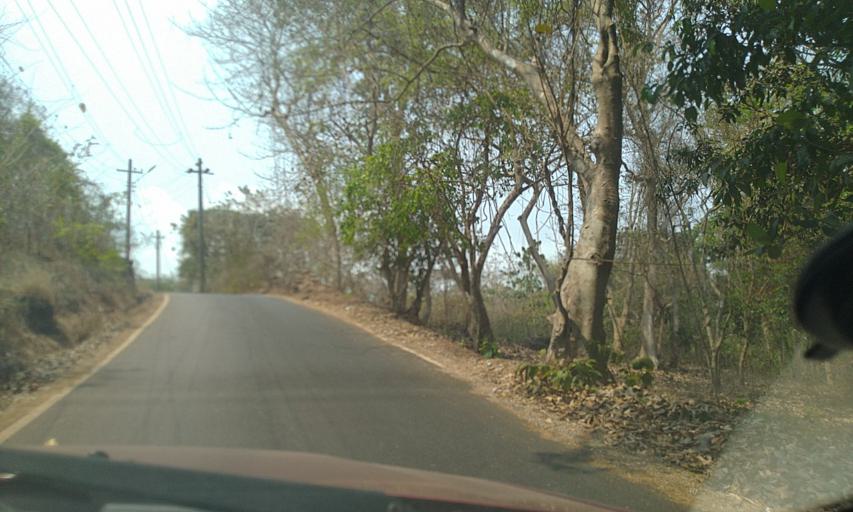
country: IN
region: Goa
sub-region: North Goa
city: Serula
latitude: 15.5235
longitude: 73.8403
